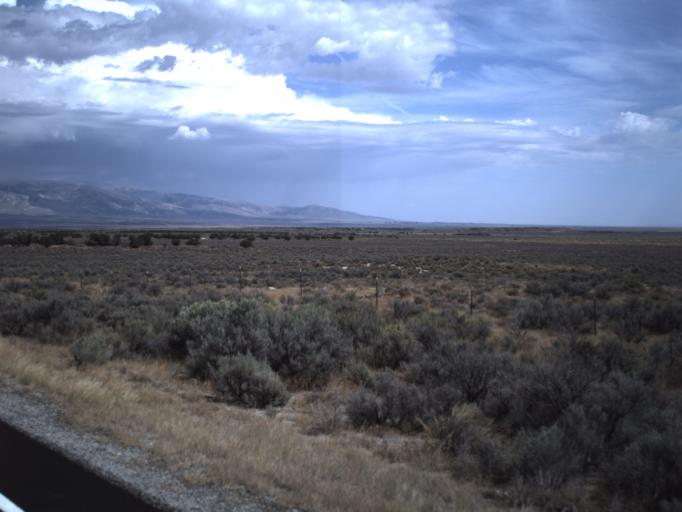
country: US
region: Idaho
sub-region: Cassia County
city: Burley
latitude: 41.7077
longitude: -113.5311
